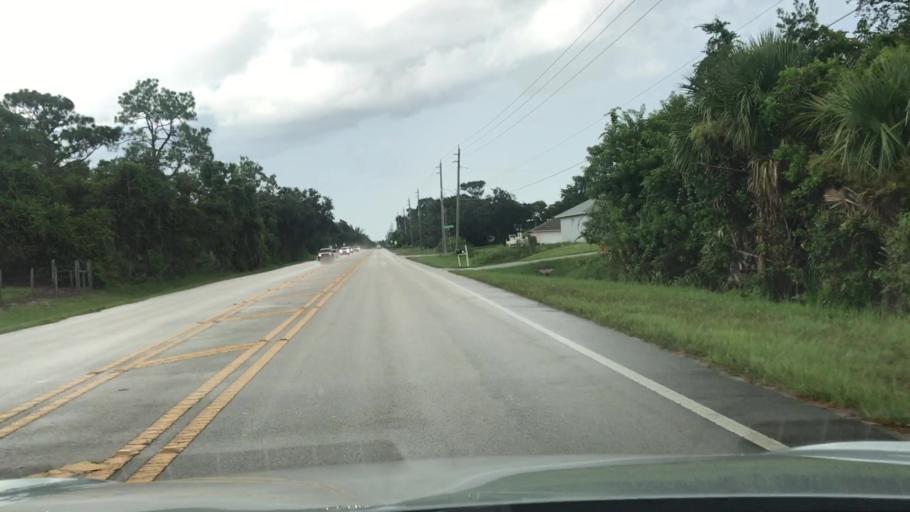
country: US
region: Florida
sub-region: Indian River County
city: Sebastian
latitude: 27.7952
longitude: -80.5005
